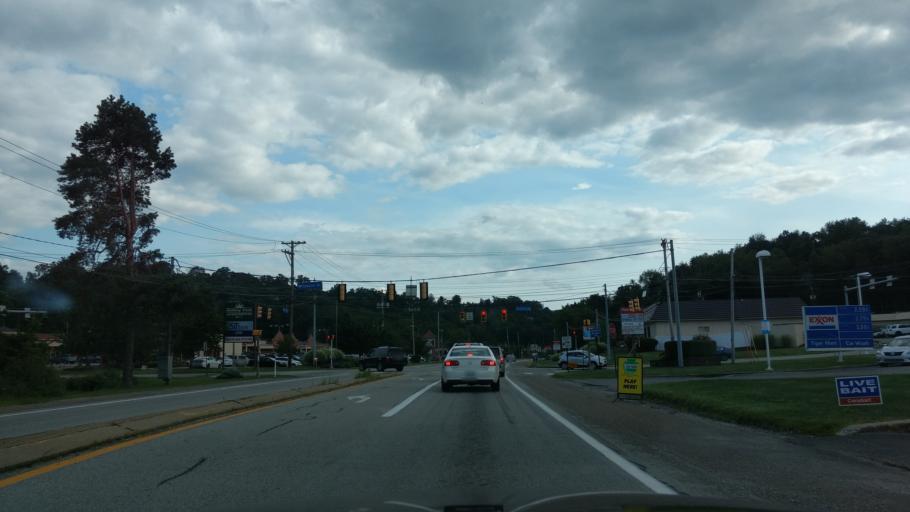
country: US
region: Pennsylvania
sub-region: Westmoreland County
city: Murrysville
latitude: 40.4642
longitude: -79.7054
